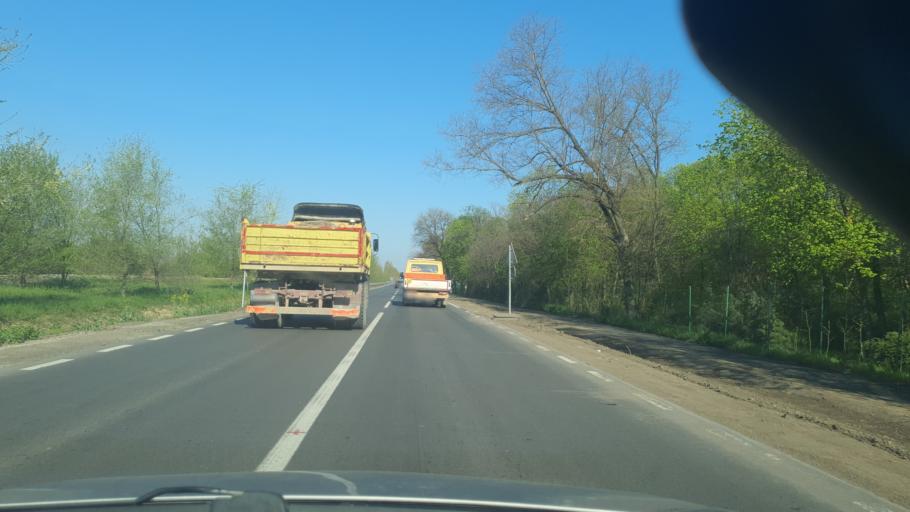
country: RS
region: Autonomna Pokrajina Vojvodina
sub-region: Juznobacki Okrug
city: Vrbas
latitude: 45.5896
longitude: 19.5962
